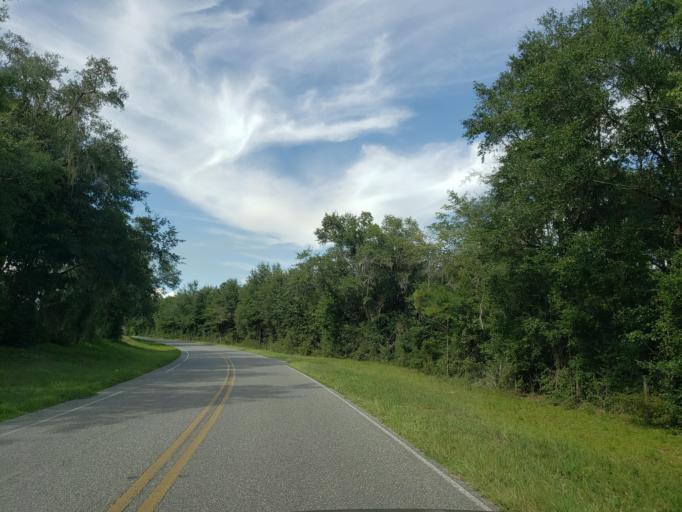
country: US
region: Georgia
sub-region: Echols County
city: Statenville
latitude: 30.6103
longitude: -83.2181
